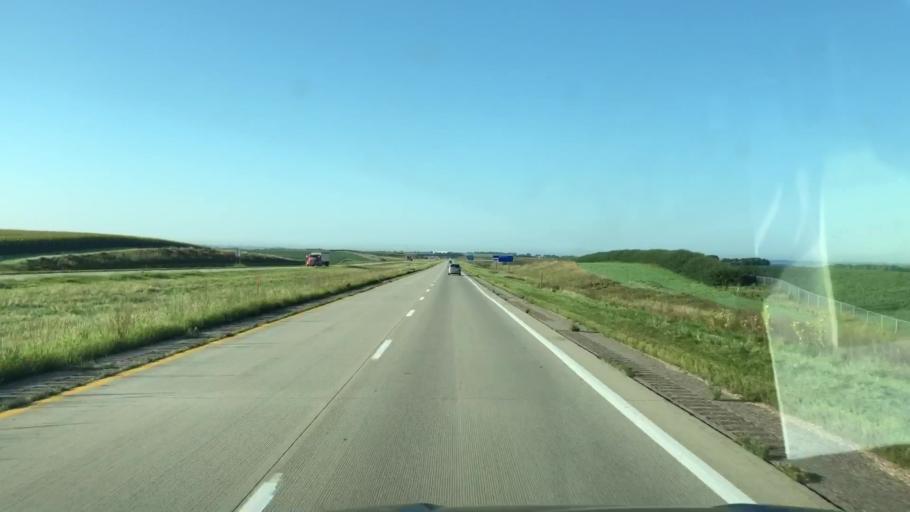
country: US
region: Iowa
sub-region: Plymouth County
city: Le Mars
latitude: 42.8051
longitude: -96.1996
